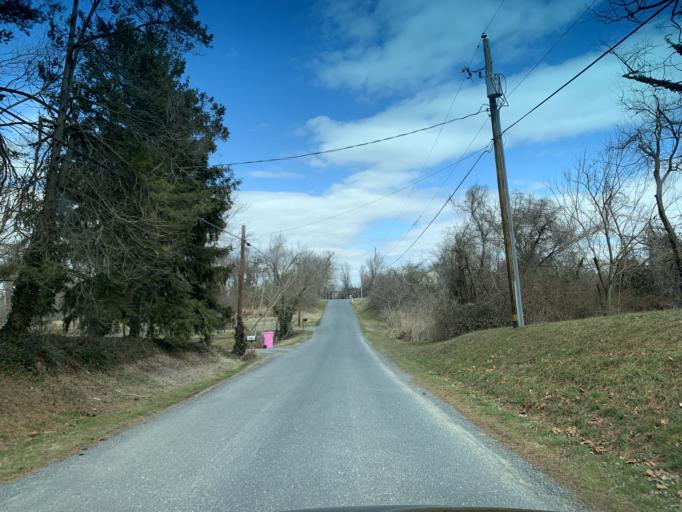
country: US
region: Maryland
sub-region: Queen Anne's County
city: Stevensville
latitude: 39.0347
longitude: -76.3094
